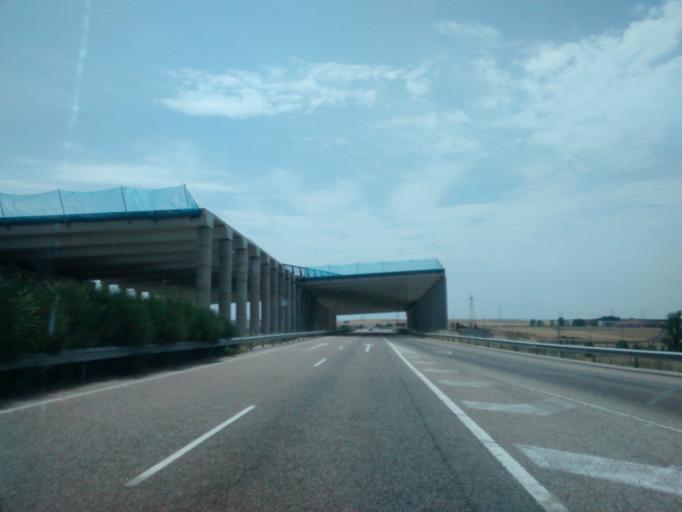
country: ES
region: Castille and Leon
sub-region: Provincia de Burgos
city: San Mames de Burgos
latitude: 42.3460
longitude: -3.7924
